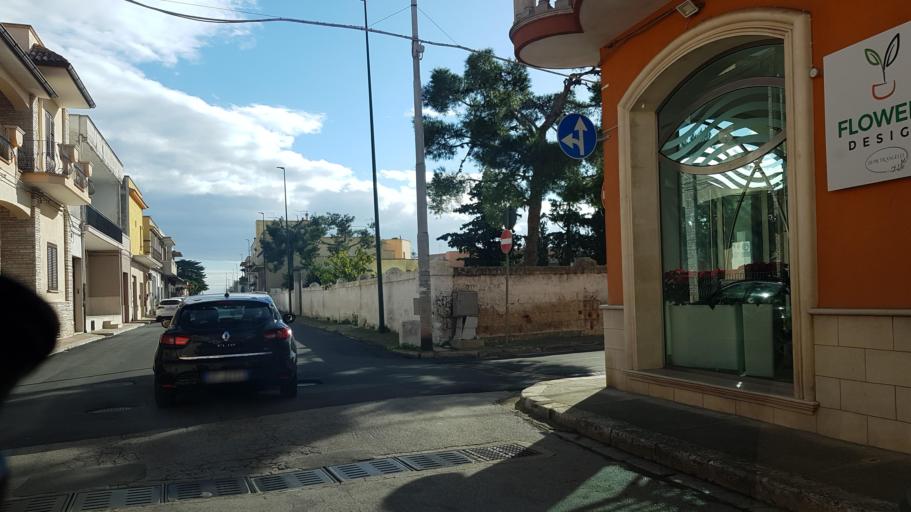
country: IT
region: Apulia
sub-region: Provincia di Brindisi
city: Torre Santa Susanna
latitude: 40.4652
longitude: 17.7436
